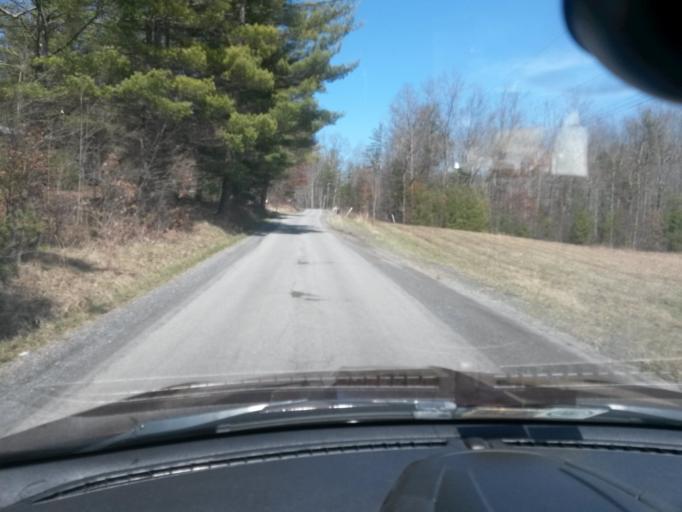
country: US
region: West Virginia
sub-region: Greenbrier County
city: White Sulphur Springs
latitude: 37.6348
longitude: -80.3392
